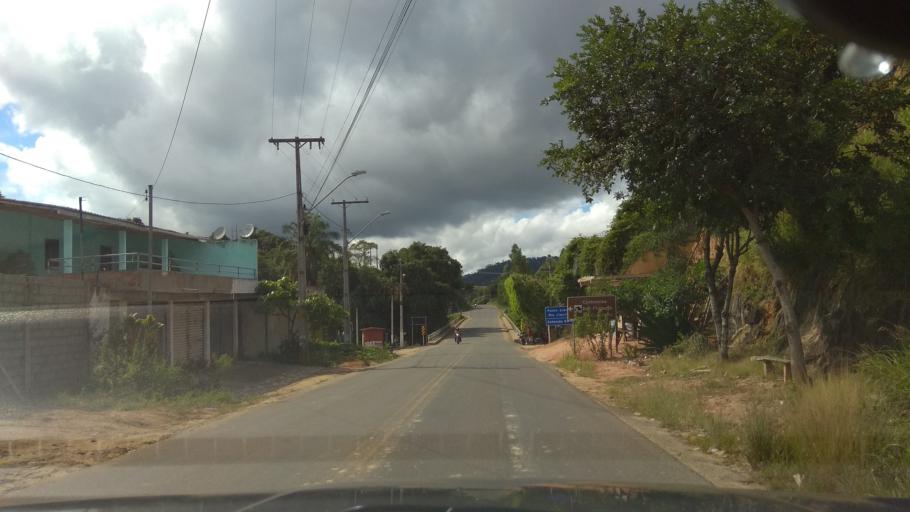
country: BR
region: Bahia
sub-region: Ubaira
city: Ubaira
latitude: -13.2550
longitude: -39.5850
